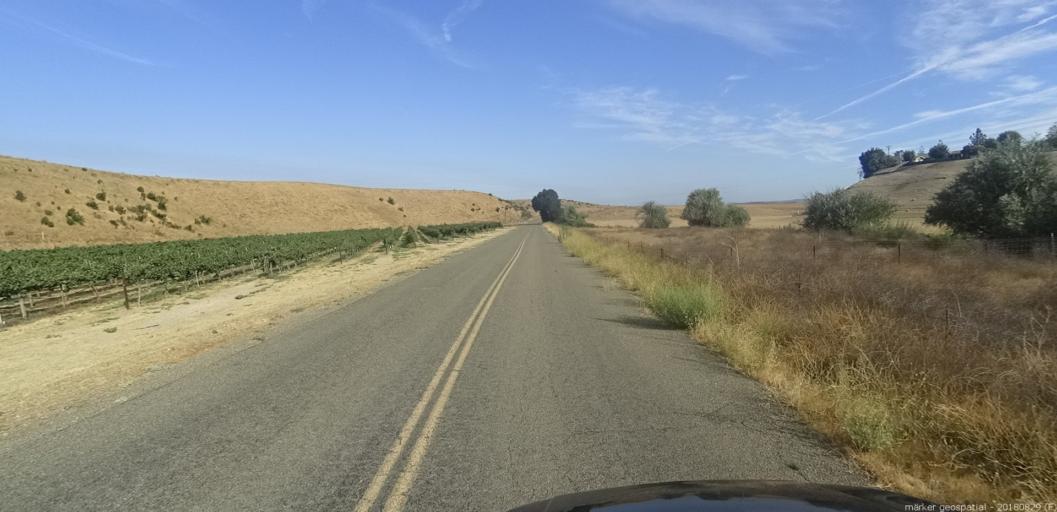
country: US
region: California
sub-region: Monterey County
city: King City
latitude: 36.0842
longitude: -121.0053
